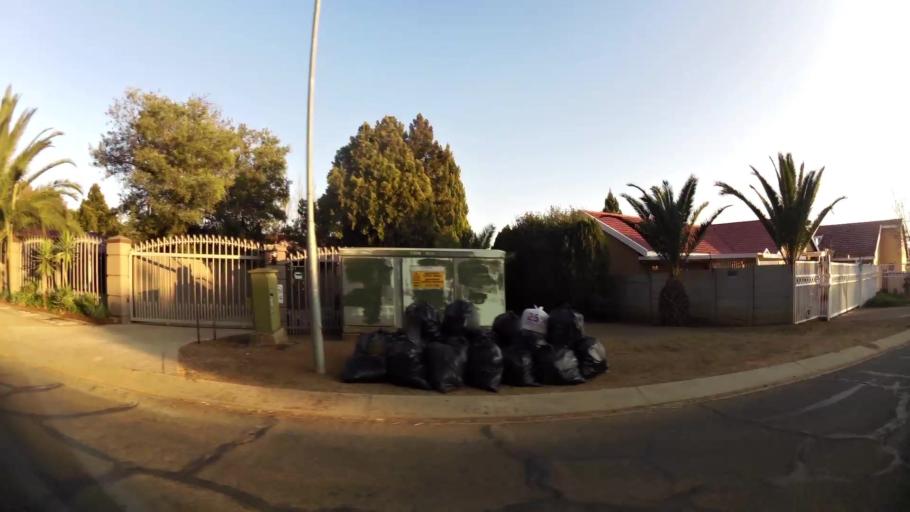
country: ZA
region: Orange Free State
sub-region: Mangaung Metropolitan Municipality
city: Bloemfontein
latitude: -29.0899
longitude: 26.1545
